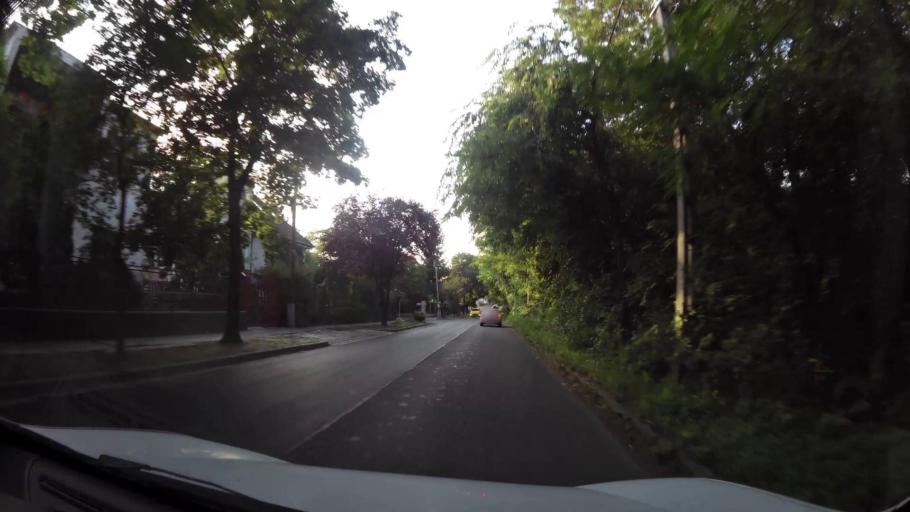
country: HU
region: Budapest
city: Budapest XVI. keruelet
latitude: 47.5051
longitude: 19.1657
